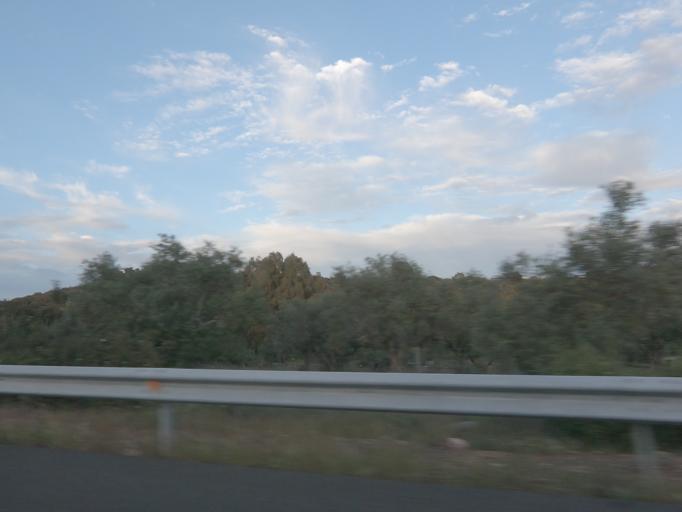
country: ES
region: Extremadura
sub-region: Provincia de Caceres
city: Alcuescar
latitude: 39.1520
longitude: -6.2748
